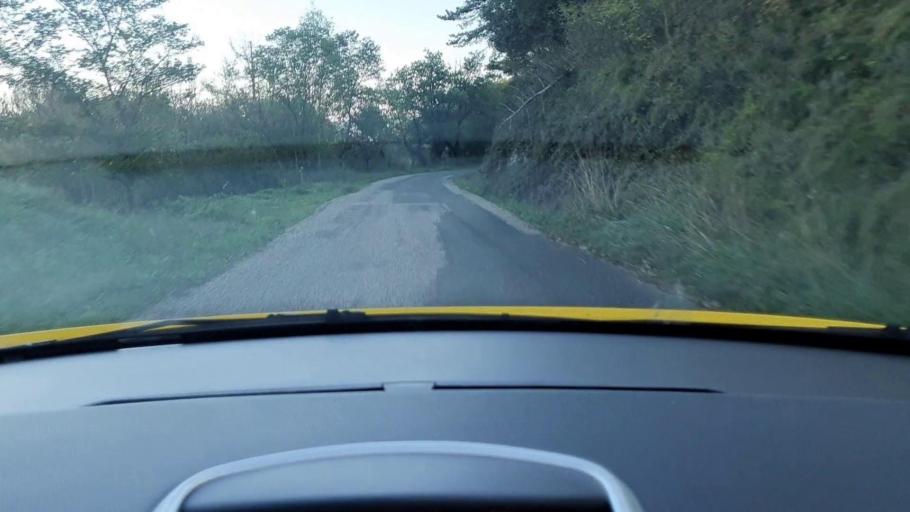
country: FR
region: Languedoc-Roussillon
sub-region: Departement du Gard
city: Sumene
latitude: 43.9751
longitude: 3.7790
